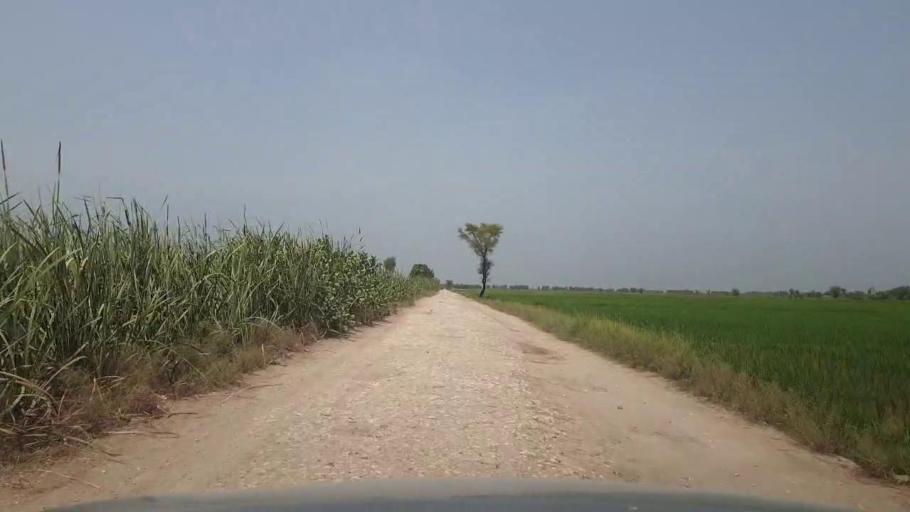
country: PK
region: Sindh
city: Garhi Yasin
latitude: 27.9345
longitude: 68.4318
